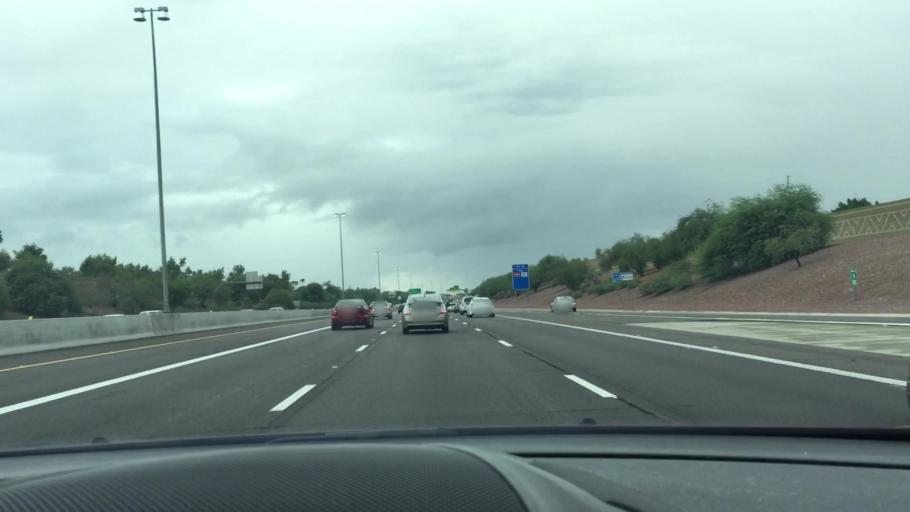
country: US
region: Arizona
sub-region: Maricopa County
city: Peoria
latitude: 33.6666
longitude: -112.2064
